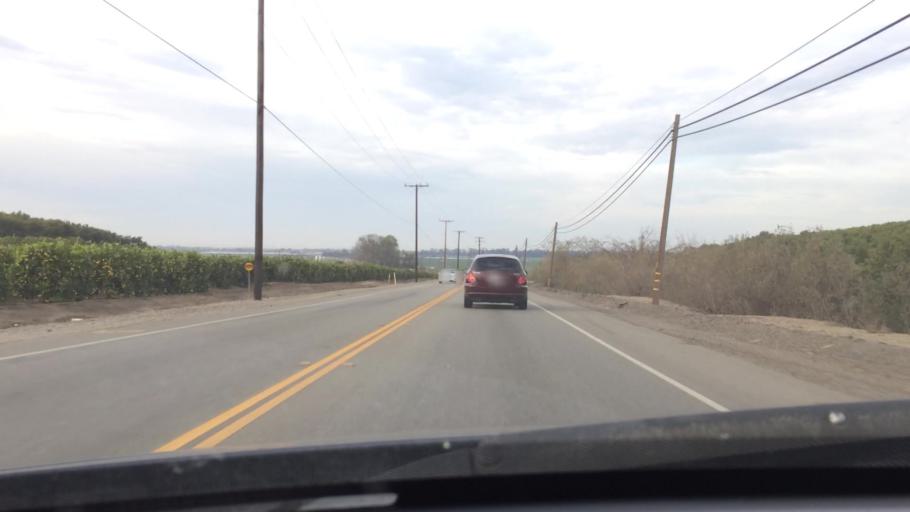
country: US
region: California
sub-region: Ventura County
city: Saticoy
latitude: 34.2606
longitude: -119.1030
